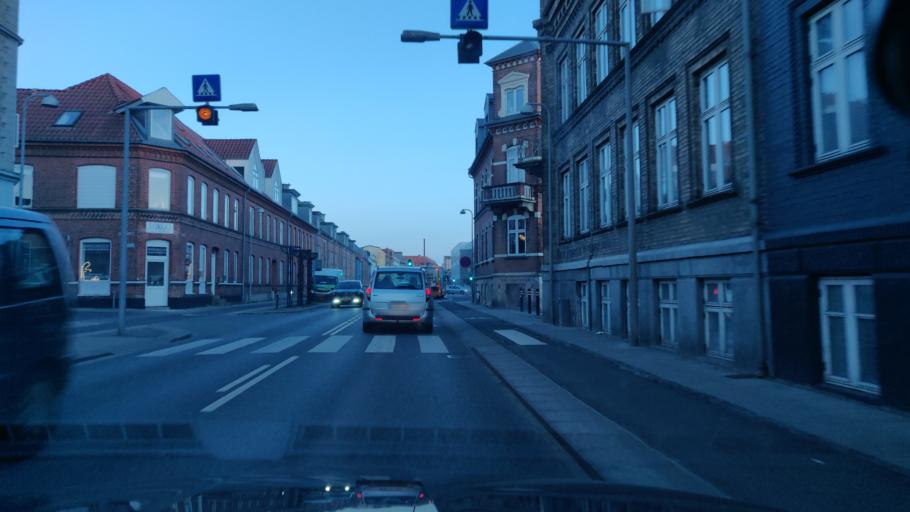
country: DK
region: North Denmark
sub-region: Alborg Kommune
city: Aalborg
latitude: 57.0615
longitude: 9.9145
